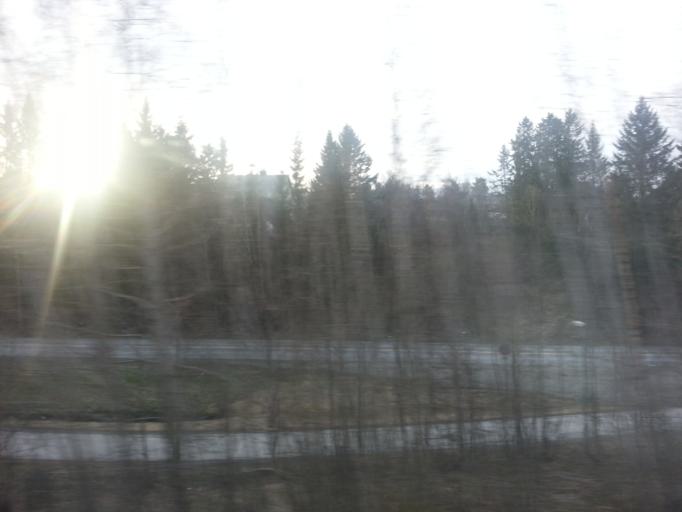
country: NO
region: Sor-Trondelag
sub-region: Trondheim
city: Trondheim
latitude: 63.3573
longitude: 10.3591
